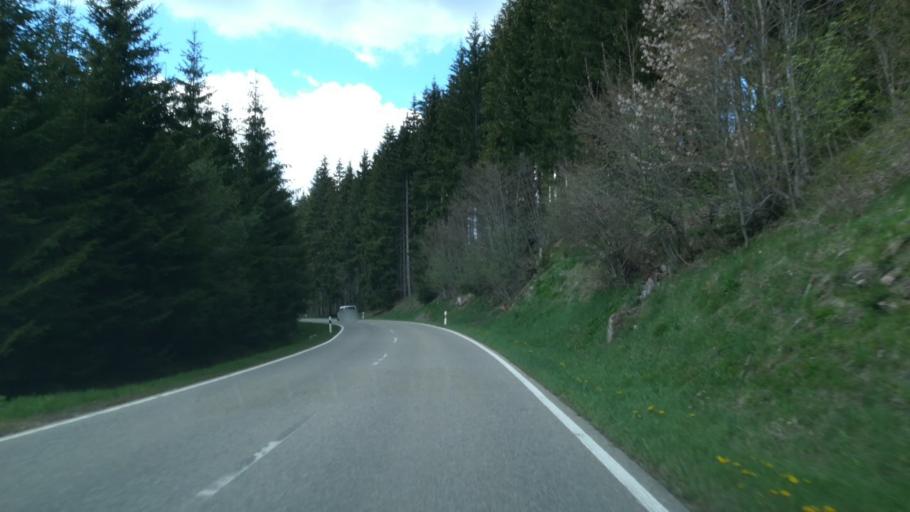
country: DE
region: Baden-Wuerttemberg
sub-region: Freiburg Region
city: Schluchsee
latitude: 47.7993
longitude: 8.2066
